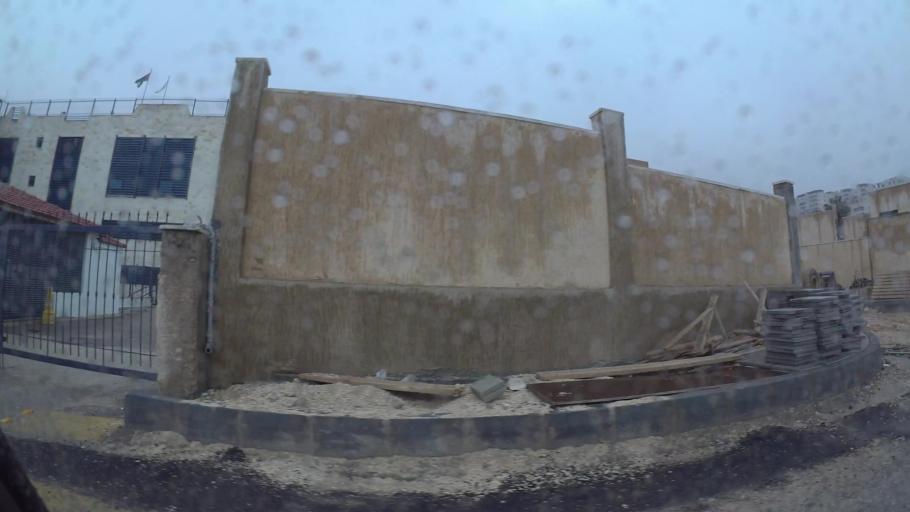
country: JO
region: Amman
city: Al Jubayhah
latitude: 32.0368
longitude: 35.8482
